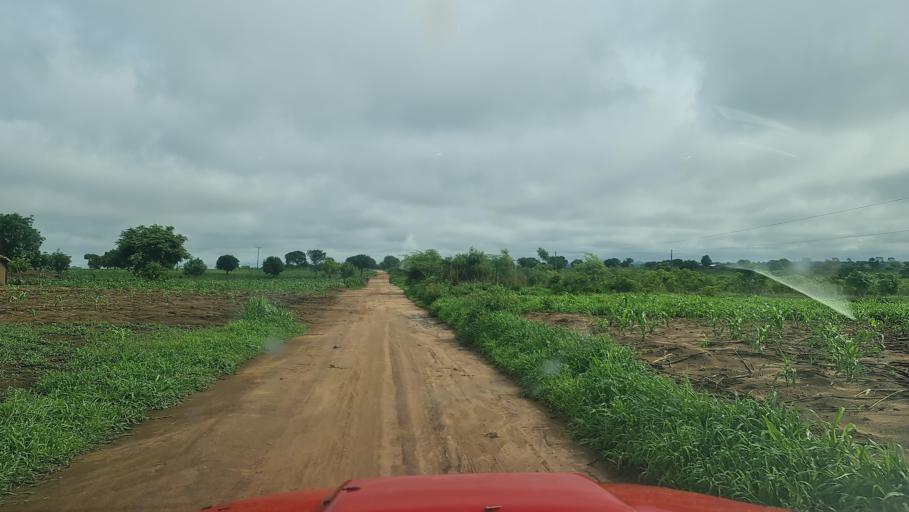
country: MW
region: Southern Region
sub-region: Nsanje District
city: Nsanje
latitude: -17.2165
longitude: 35.6755
